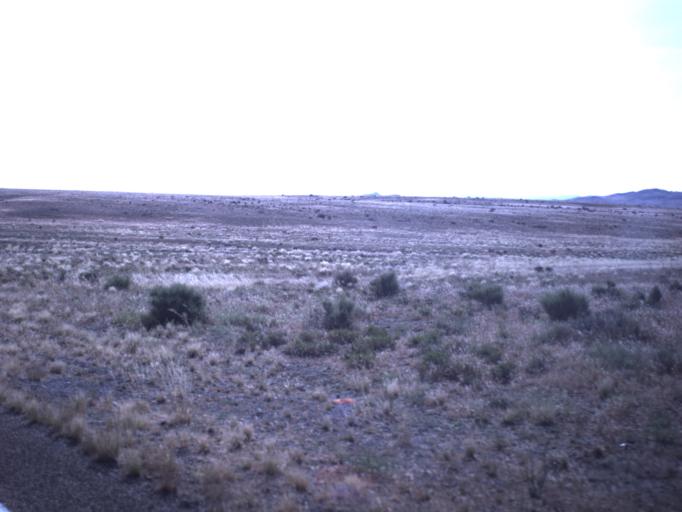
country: US
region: Utah
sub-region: Beaver County
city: Milford
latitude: 38.8006
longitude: -112.8912
